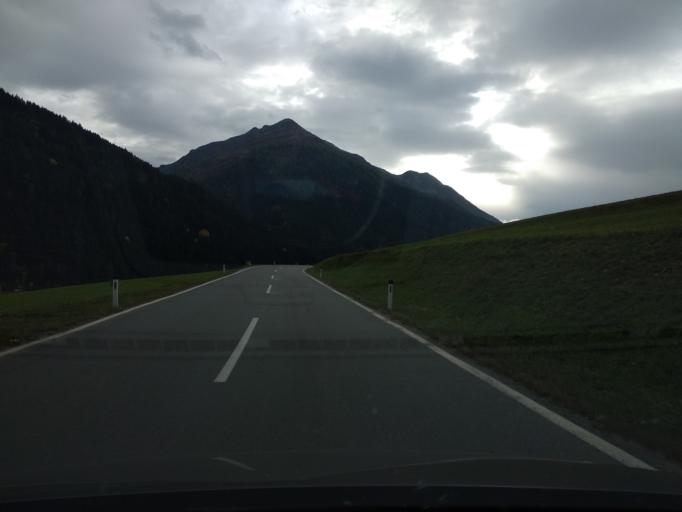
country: AT
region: Tyrol
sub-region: Politischer Bezirk Landeck
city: Flirsch
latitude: 47.1517
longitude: 10.3548
